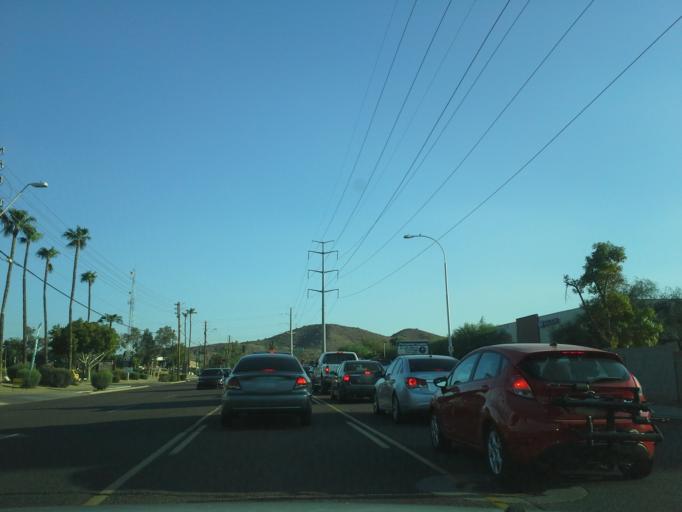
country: US
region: Arizona
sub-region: Maricopa County
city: Guadalupe
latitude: 33.3799
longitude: -111.9784
